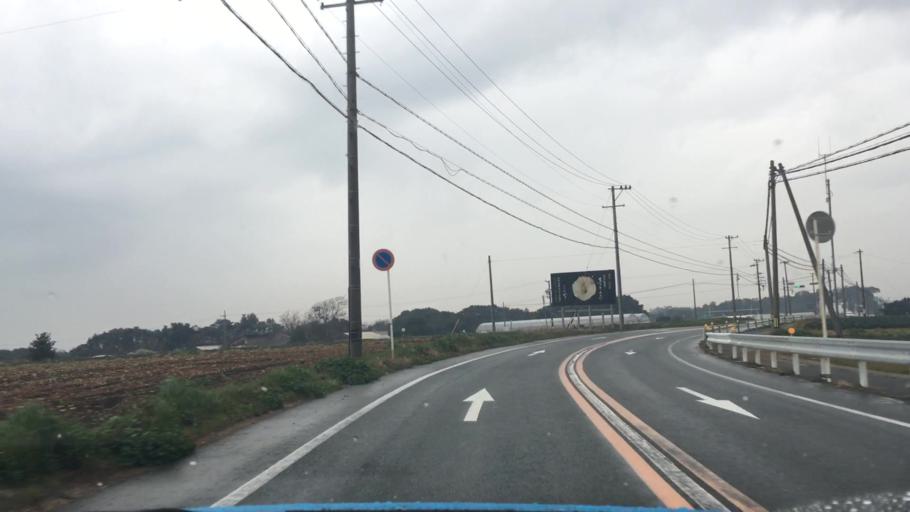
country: JP
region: Aichi
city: Toyohashi
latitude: 34.6639
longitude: 137.3743
